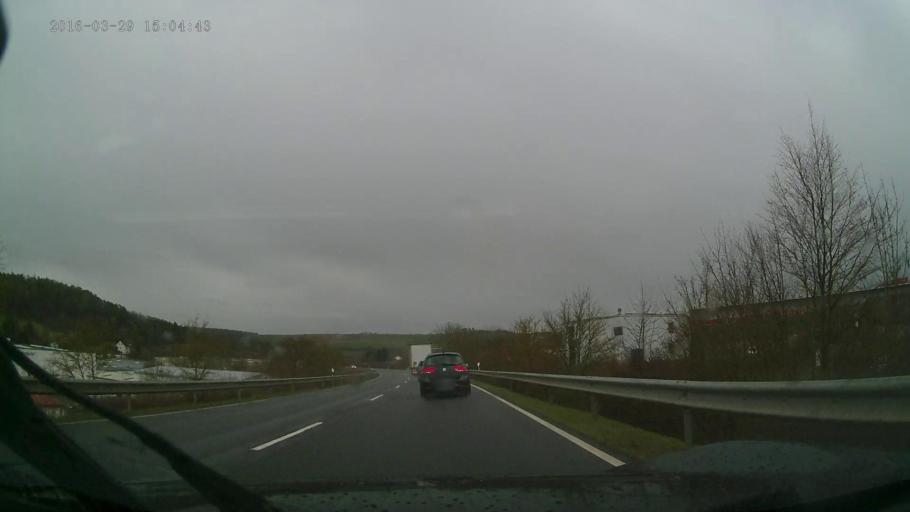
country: DE
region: Baden-Wuerttemberg
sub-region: Karlsruhe Region
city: Buchen
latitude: 49.5304
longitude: 9.3377
